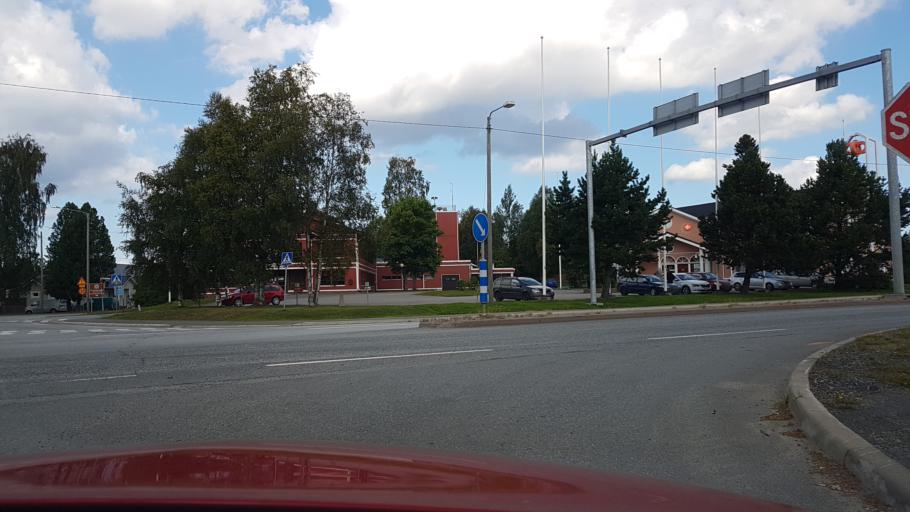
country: FI
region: Northern Ostrobothnia
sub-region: Ylivieska
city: Himanka
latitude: 64.0615
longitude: 23.6549
